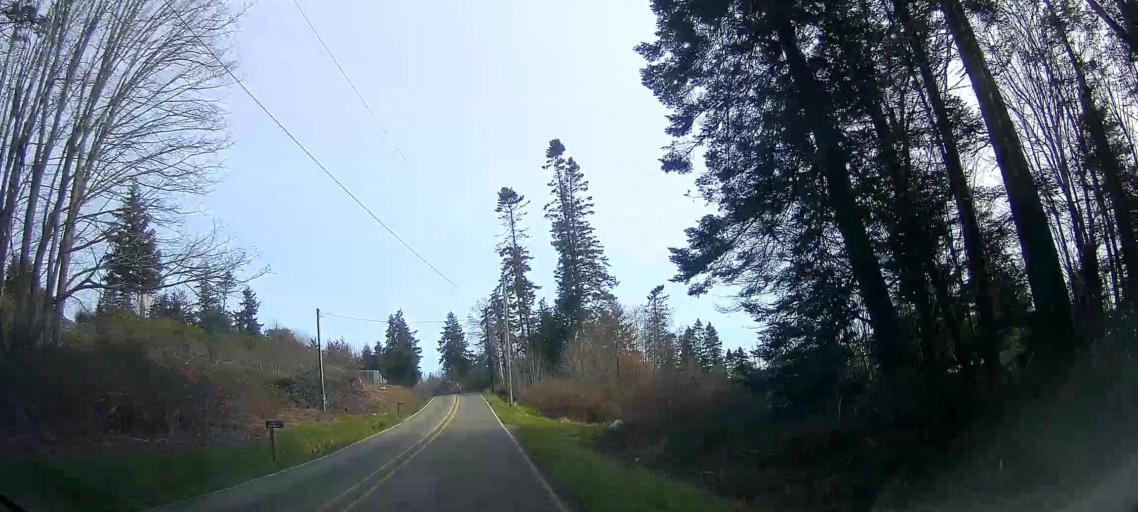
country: US
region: Washington
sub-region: Island County
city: Langley
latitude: 48.0583
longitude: -122.3702
